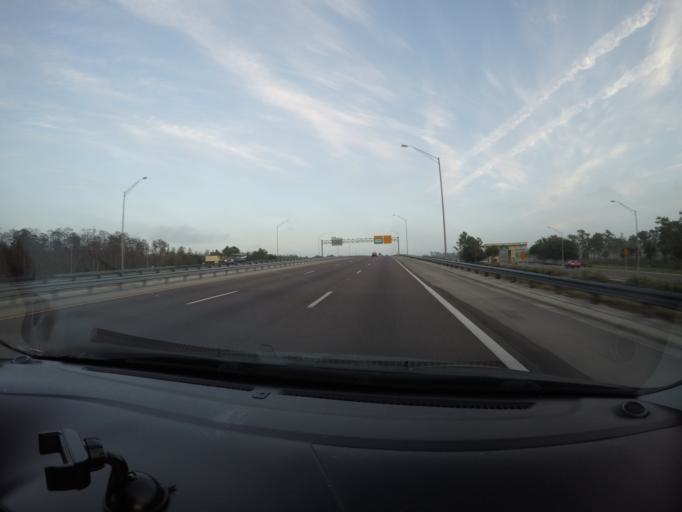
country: US
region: Florida
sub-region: Orange County
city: Azalea Park
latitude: 28.4750
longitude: -81.2387
